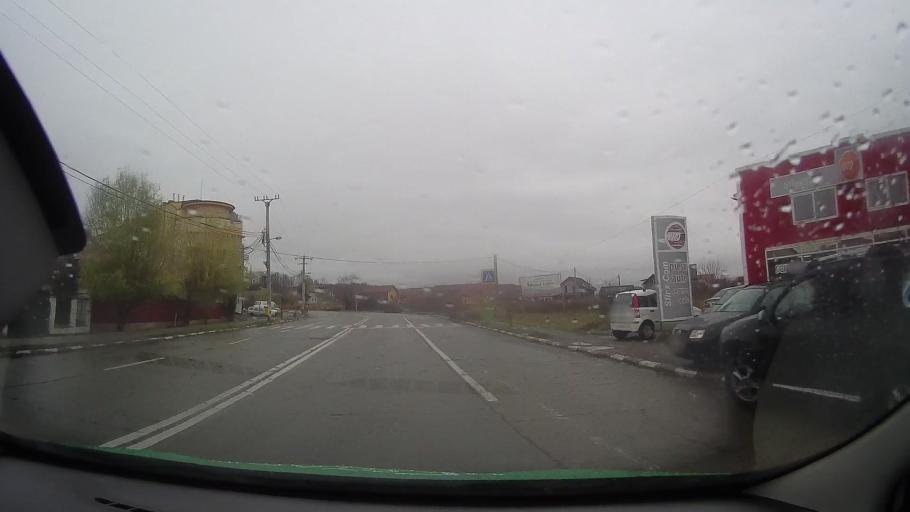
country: RO
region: Mures
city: Reghin-Sat
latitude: 46.7891
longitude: 24.7156
